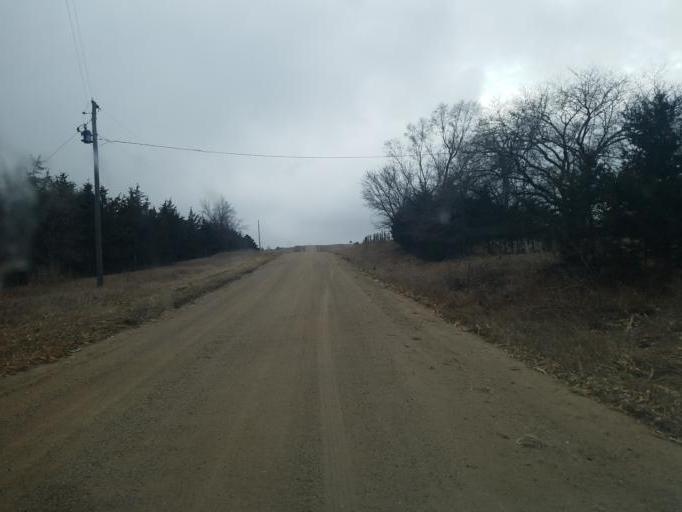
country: US
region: Nebraska
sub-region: Knox County
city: Center
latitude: 42.5247
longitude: -97.7990
